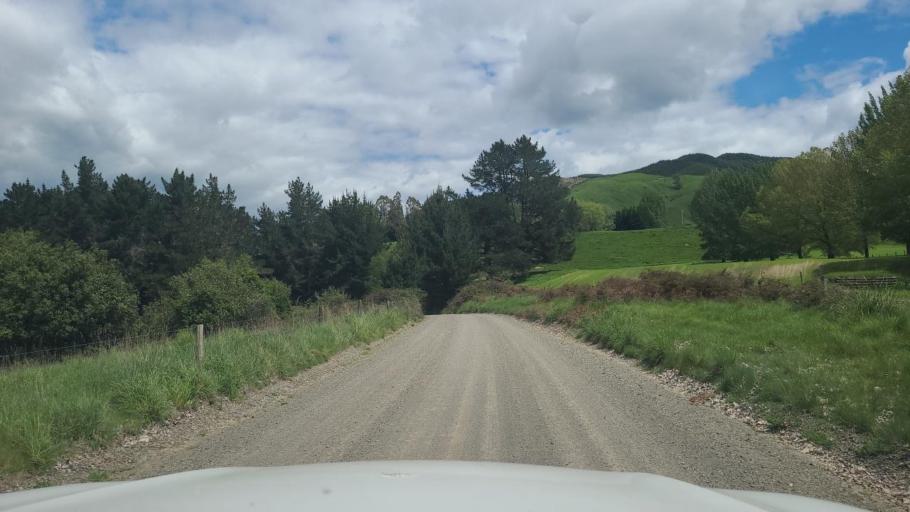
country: NZ
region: Hawke's Bay
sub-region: Napier City
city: Taradale
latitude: -39.1873
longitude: 176.6272
